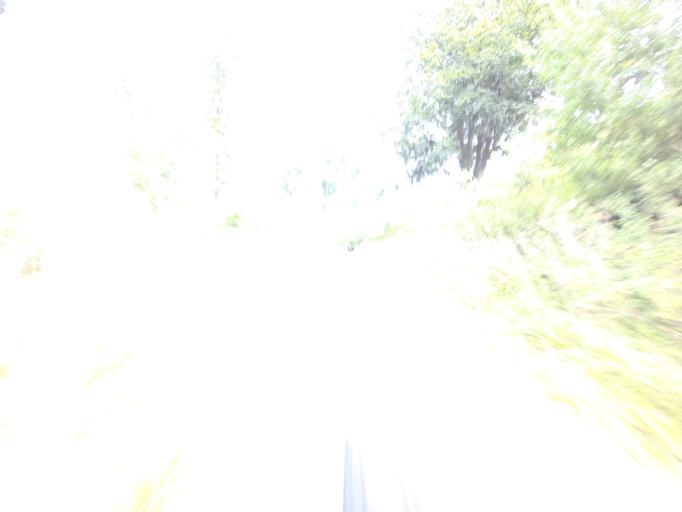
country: DK
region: Central Jutland
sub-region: Syddjurs Kommune
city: Ryomgard
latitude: 56.3813
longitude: 10.5300
